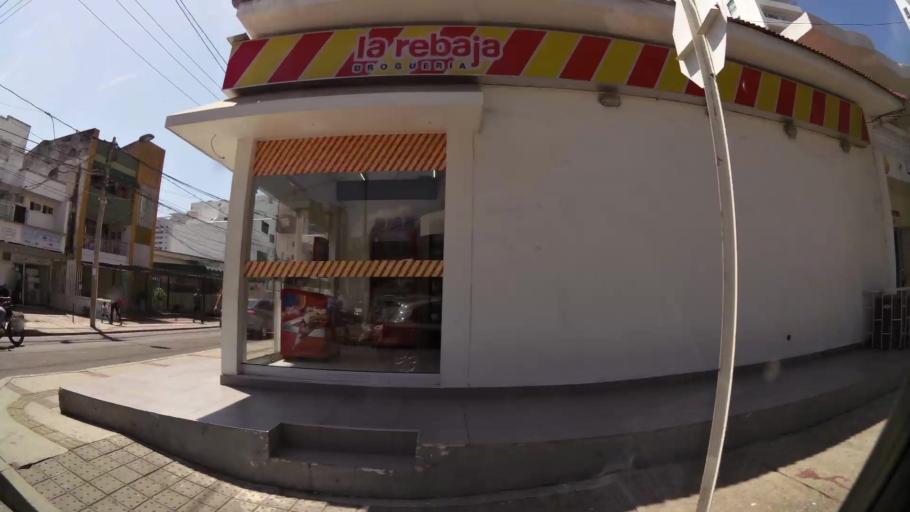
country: CO
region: Bolivar
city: Cartagena
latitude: 10.4139
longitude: -75.5331
